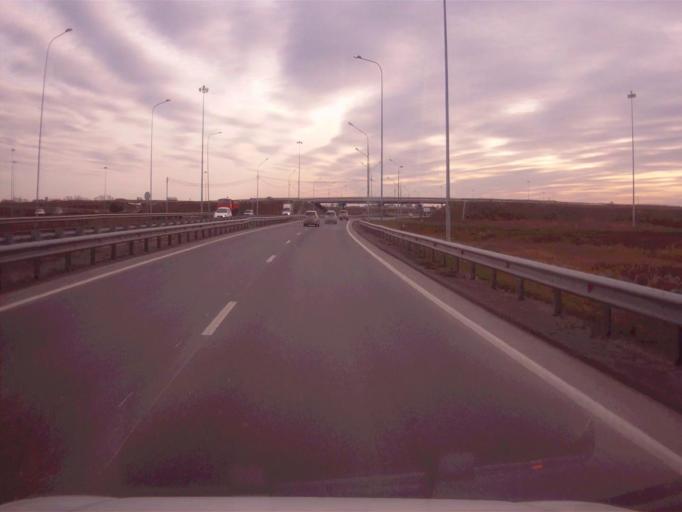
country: RU
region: Chelyabinsk
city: Novosineglazovskiy
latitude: 55.0045
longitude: 61.4540
